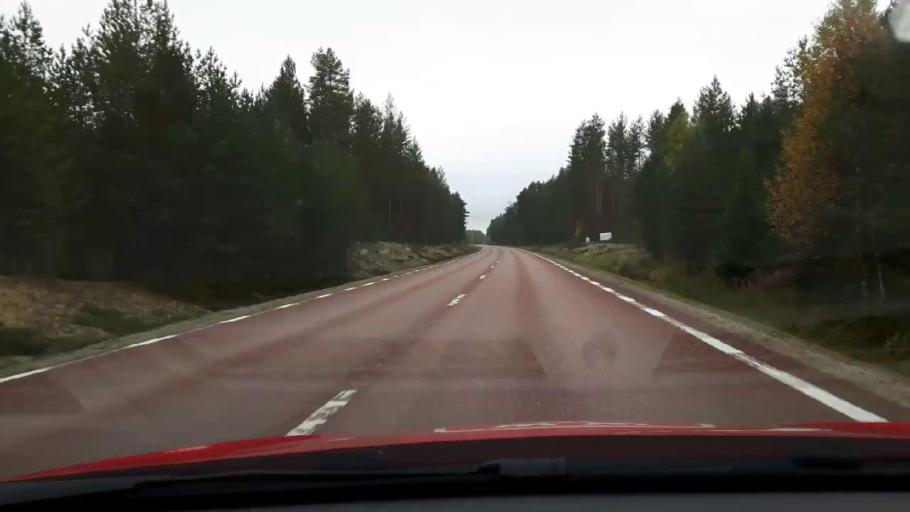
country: SE
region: Gaevleborg
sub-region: Ljusdals Kommun
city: Farila
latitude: 61.8319
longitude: 15.7513
